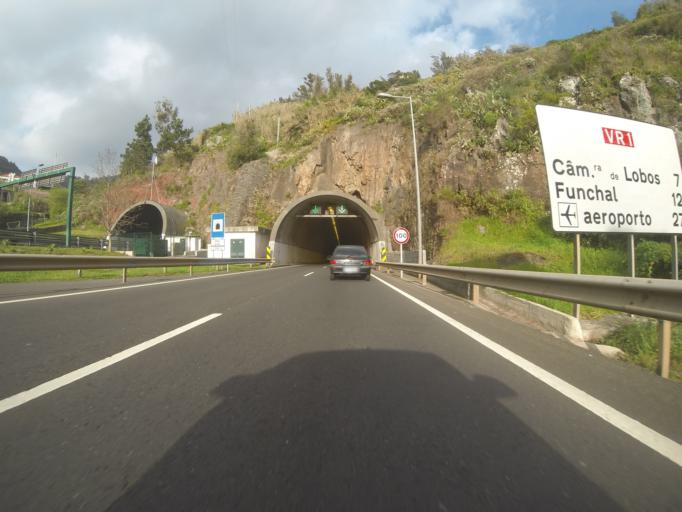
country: PT
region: Madeira
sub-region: Ribeira Brava
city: Campanario
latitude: 32.6591
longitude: -17.0091
